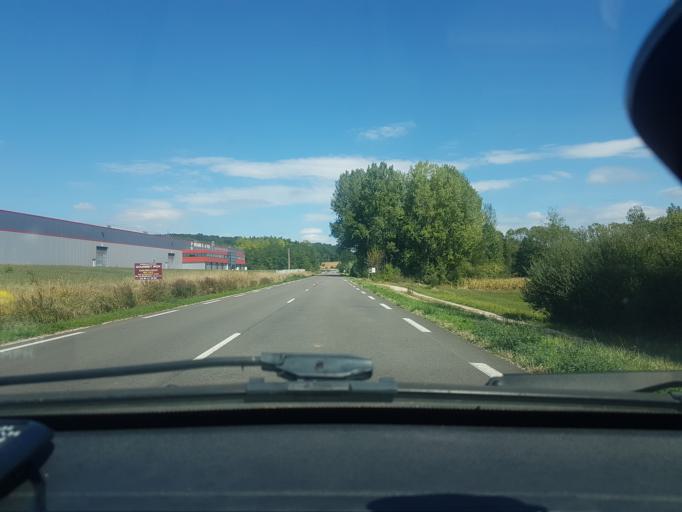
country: FR
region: Franche-Comte
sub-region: Departement de la Haute-Saone
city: Gray-la-Ville
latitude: 47.4419
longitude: 5.5483
